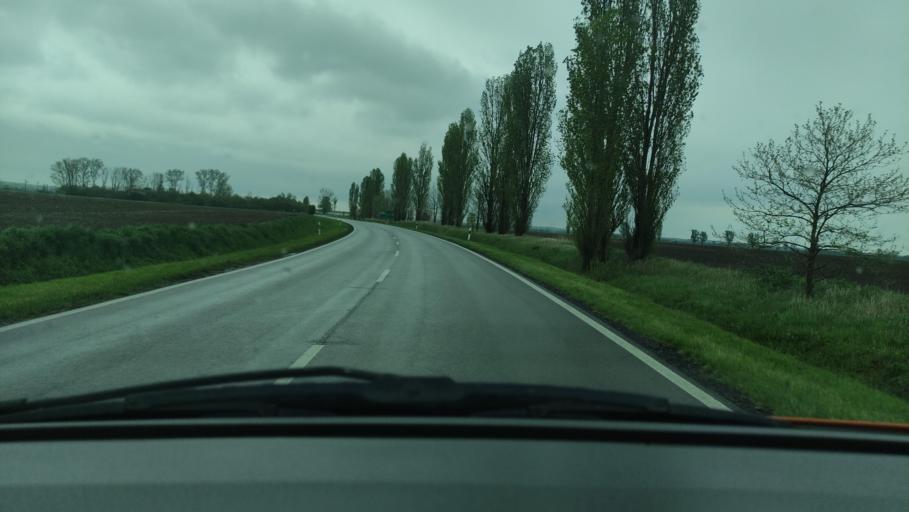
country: HU
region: Baranya
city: Mohacs
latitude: 45.9733
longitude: 18.6678
